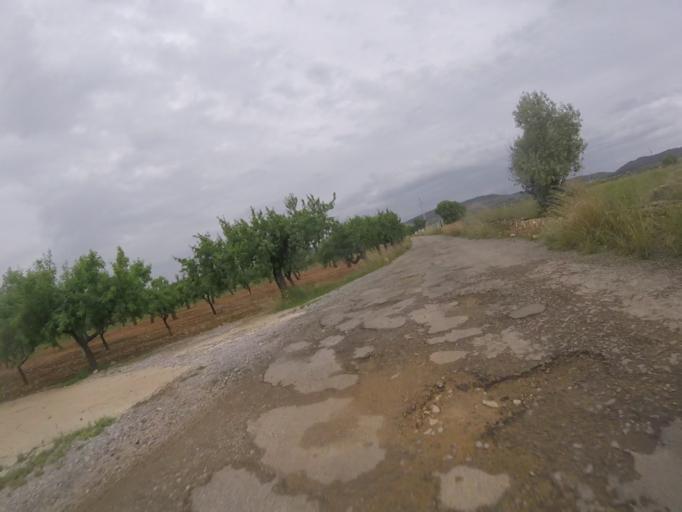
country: ES
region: Valencia
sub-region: Provincia de Castello
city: Torreblanca
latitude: 40.2208
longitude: 0.2133
